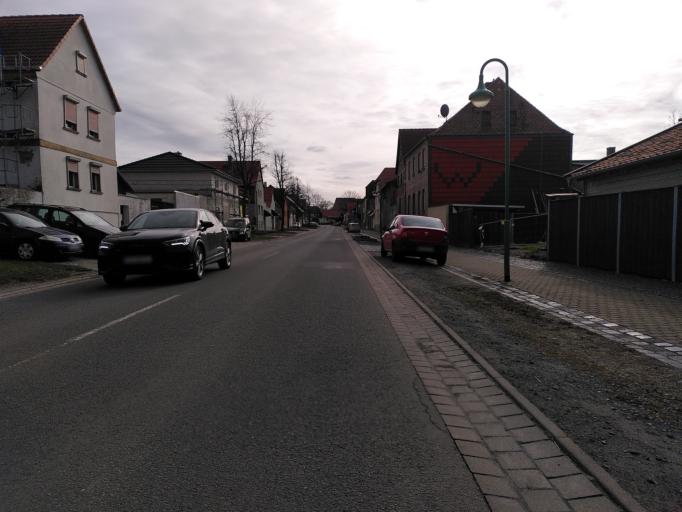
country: DE
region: Saxony-Anhalt
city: Ballenstedt
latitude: 51.7684
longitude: 11.2447
